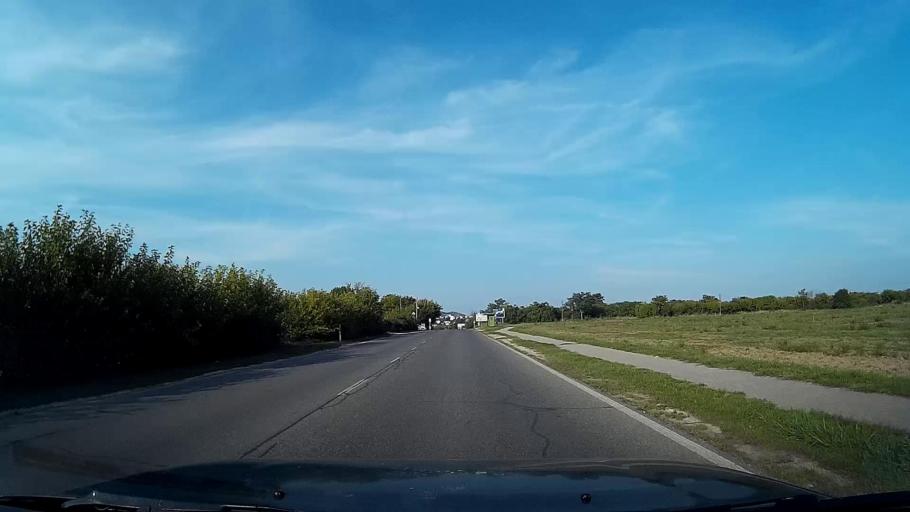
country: HU
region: Pest
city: Budaors
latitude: 47.4519
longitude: 18.9902
